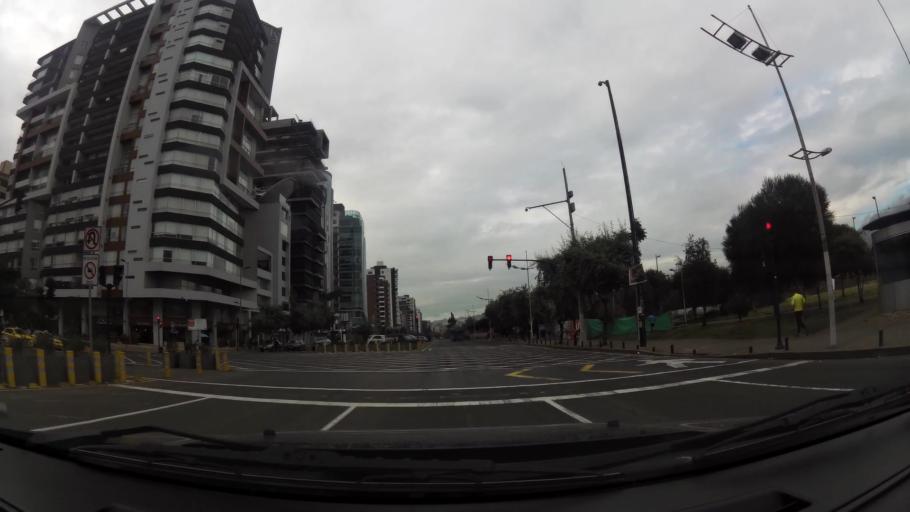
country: EC
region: Pichincha
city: Quito
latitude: -0.1812
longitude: -78.4819
